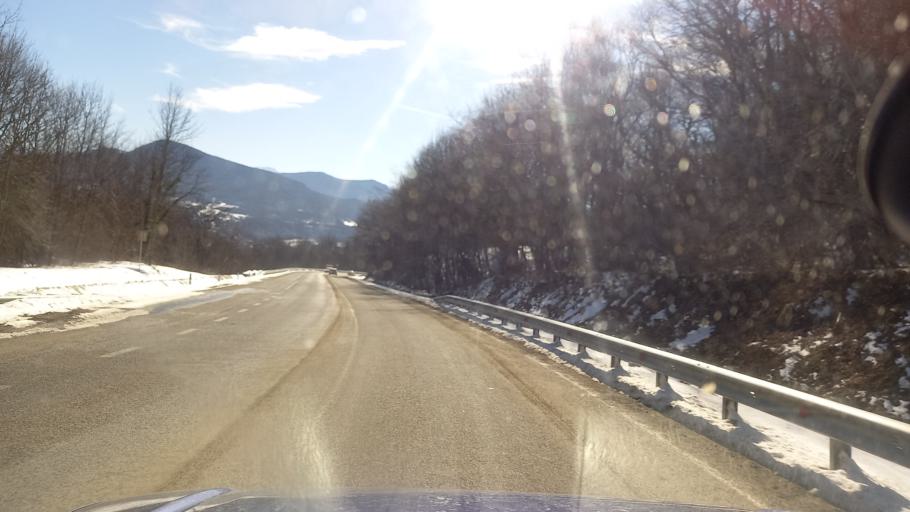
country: RU
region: Adygeya
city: Kamennomostskiy
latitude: 44.2447
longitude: 40.1906
